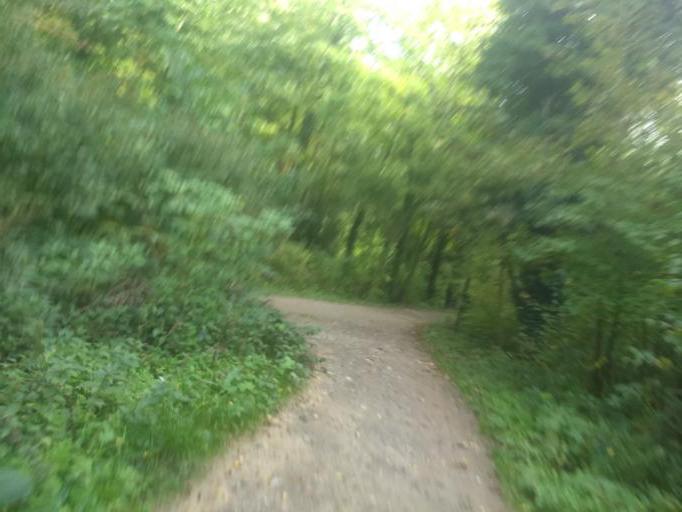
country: FR
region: Nord-Pas-de-Calais
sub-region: Departement du Pas-de-Calais
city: Achicourt
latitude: 50.2803
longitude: 2.7602
